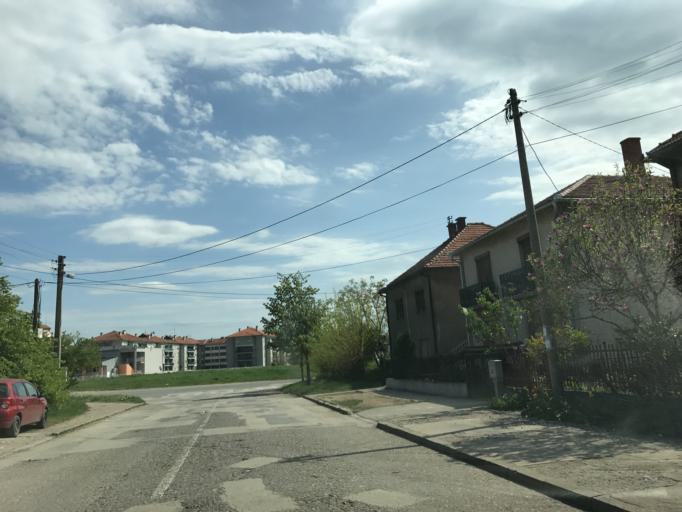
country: RS
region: Central Serbia
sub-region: Zajecarski Okrug
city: Zajecar
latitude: 43.9096
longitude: 22.2689
